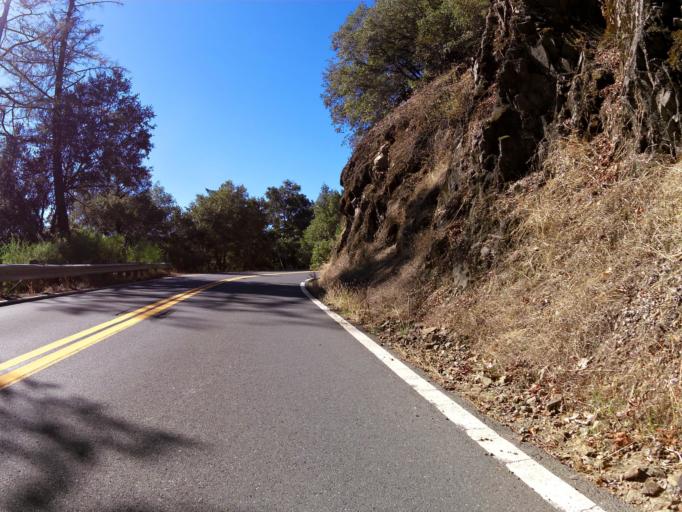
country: US
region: California
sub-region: Humboldt County
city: Redway
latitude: 39.8602
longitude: -123.7275
